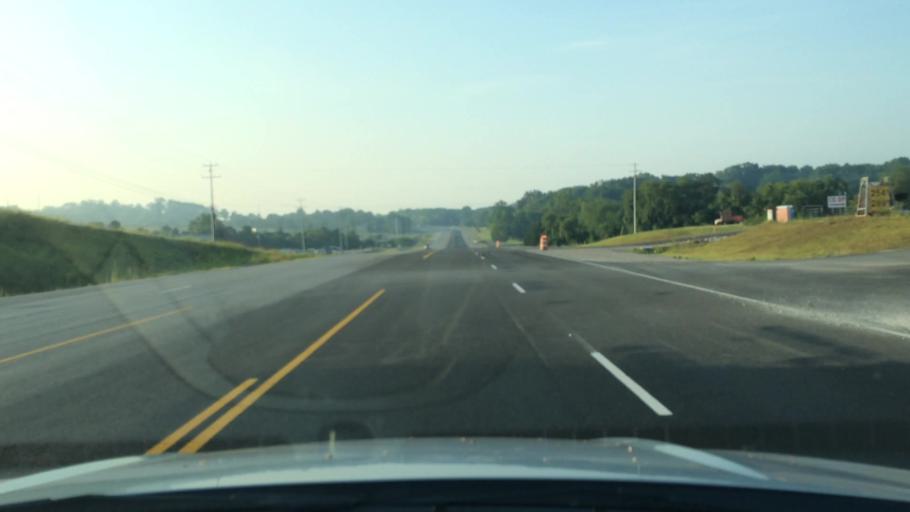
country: US
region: Tennessee
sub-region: Giles County
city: Pulaski
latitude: 35.1530
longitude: -87.0043
